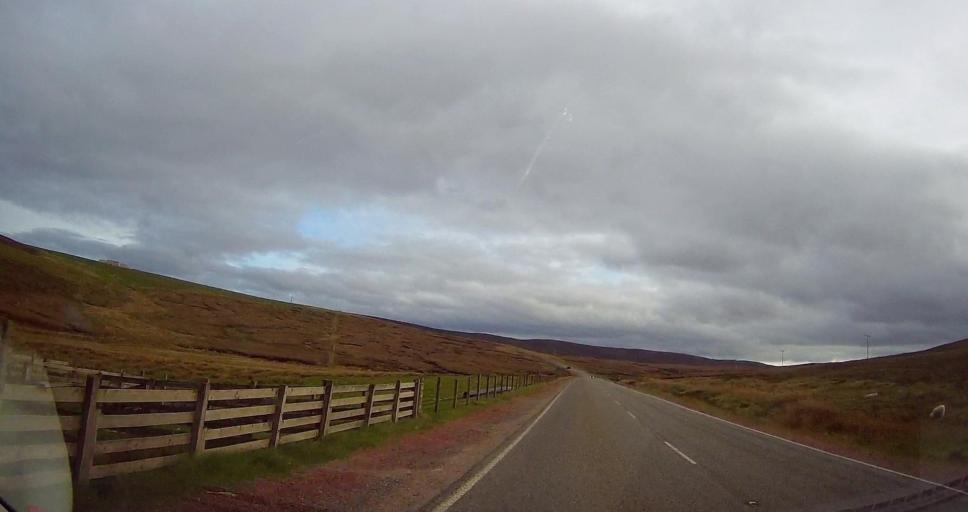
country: GB
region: Scotland
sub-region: Shetland Islands
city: Lerwick
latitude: 60.4580
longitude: -1.2107
